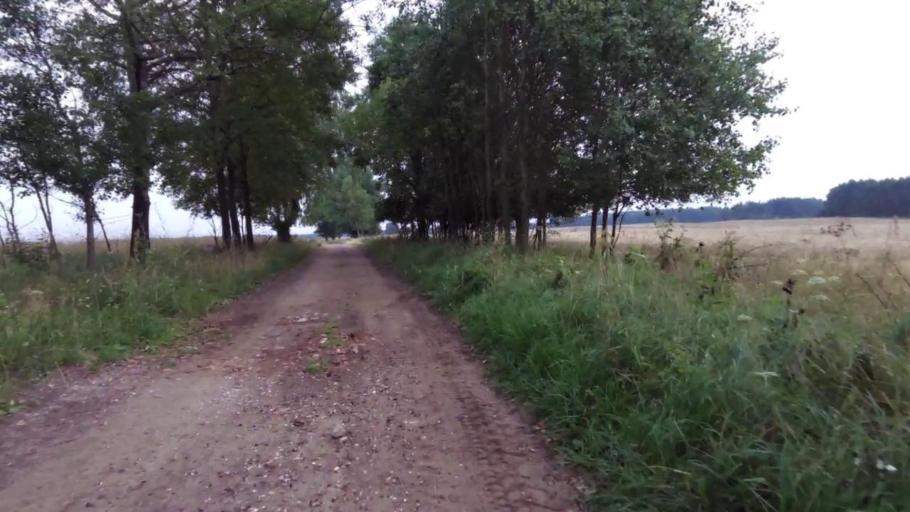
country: PL
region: West Pomeranian Voivodeship
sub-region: Powiat szczecinecki
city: Lubowo
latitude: 53.6124
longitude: 16.3424
